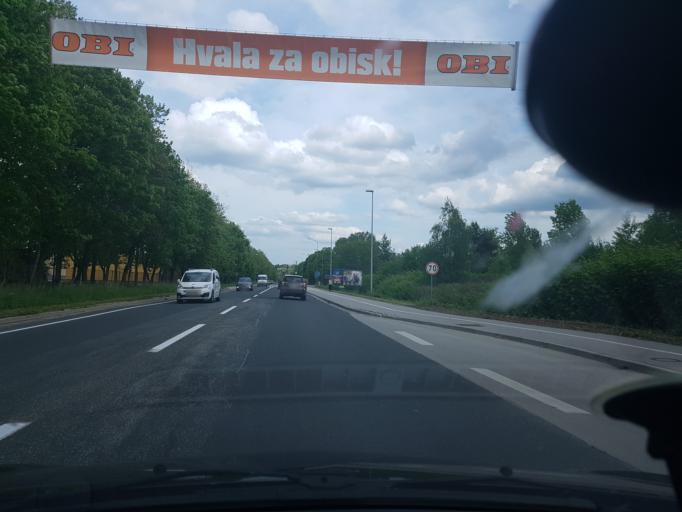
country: SI
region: Celje
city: Trnovlje pri Celju
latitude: 46.2350
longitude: 15.2848
